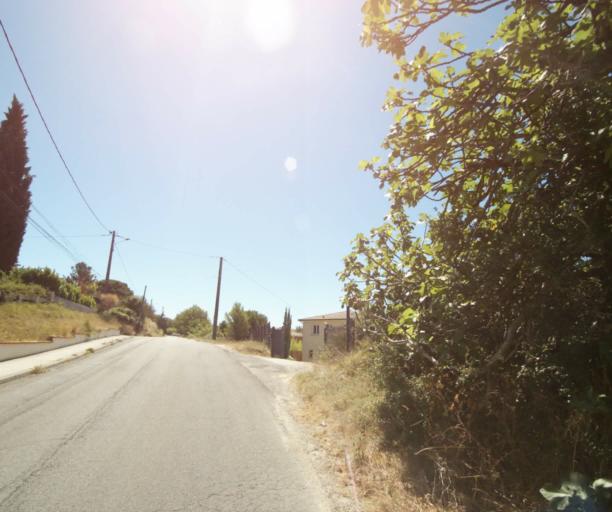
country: FR
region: Midi-Pyrenees
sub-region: Departement de la Haute-Garonne
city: Castanet-Tolosan
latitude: 43.5081
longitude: 1.4988
